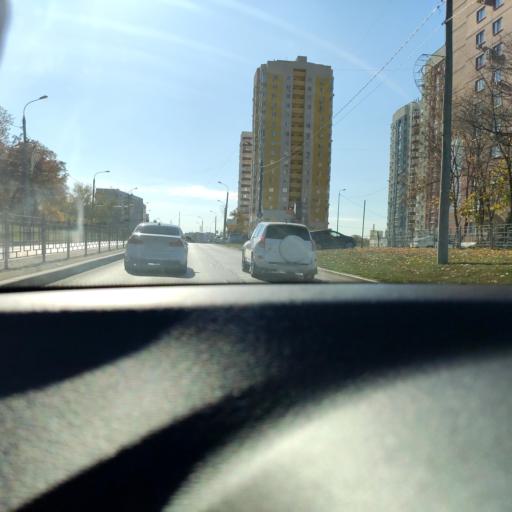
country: RU
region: Samara
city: Samara
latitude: 53.2562
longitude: 50.2034
